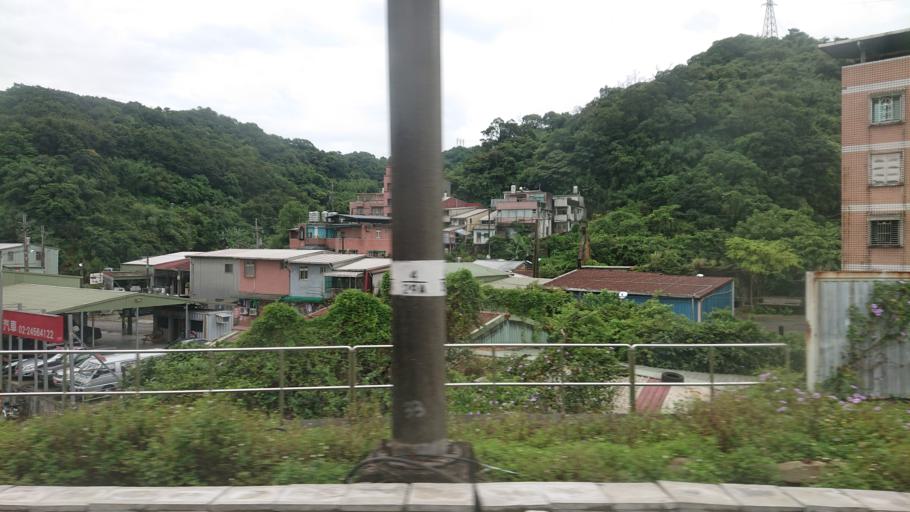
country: TW
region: Taiwan
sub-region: Keelung
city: Keelung
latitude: 25.1022
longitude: 121.7251
